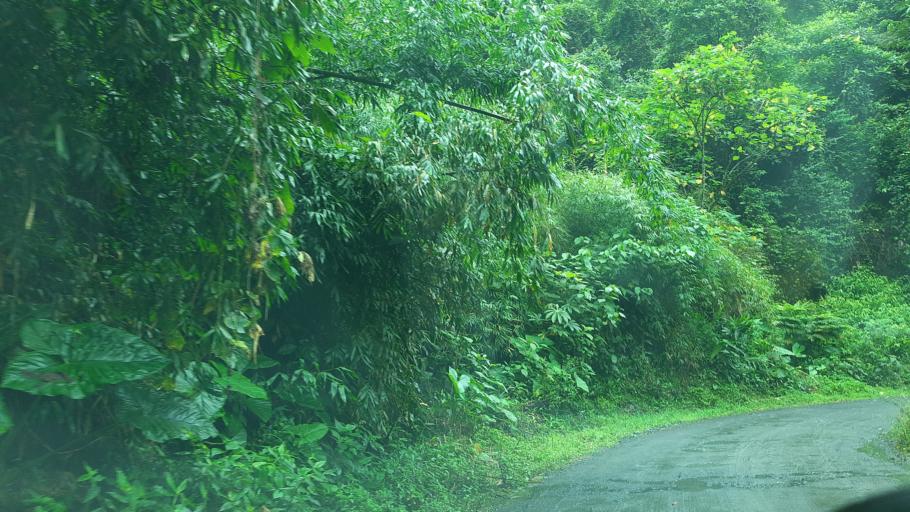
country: CO
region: Boyaca
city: Chivor
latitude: 4.9117
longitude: -73.3096
